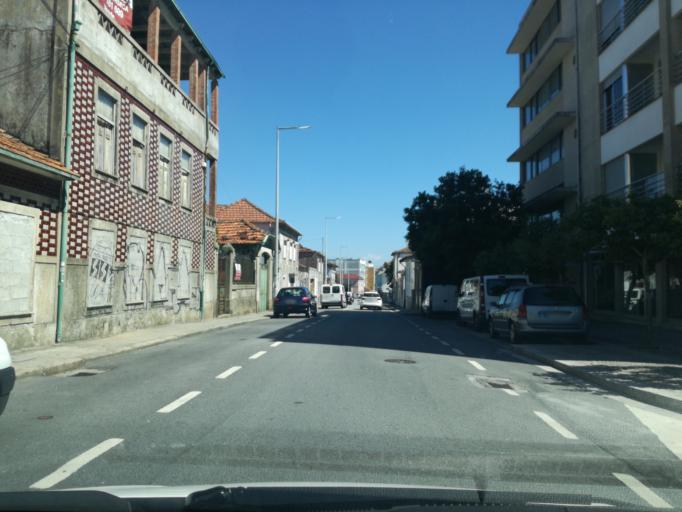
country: PT
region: Porto
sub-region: Maia
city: Maia
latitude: 41.2294
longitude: -8.6190
